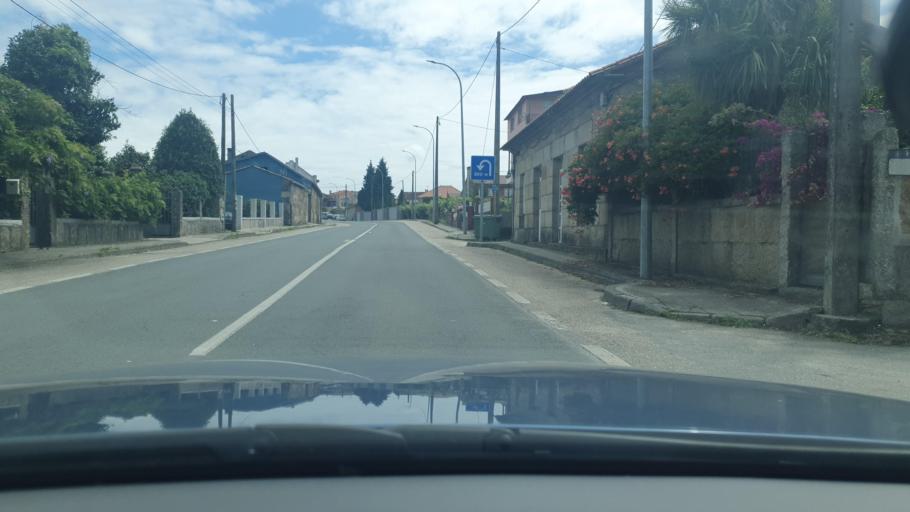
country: ES
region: Galicia
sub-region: Provincia de Pontevedra
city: Cambados
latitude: 42.4855
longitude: -8.8038
